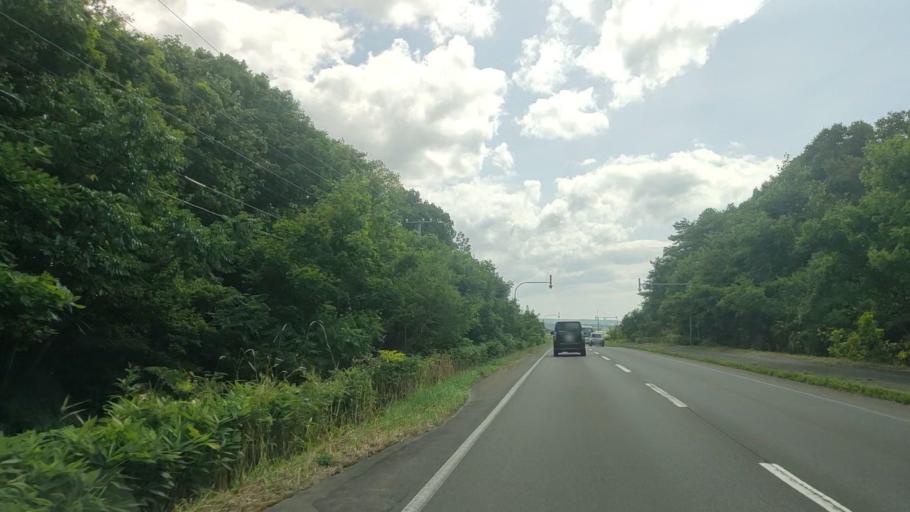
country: JP
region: Hokkaido
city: Makubetsu
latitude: 44.7639
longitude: 141.7936
